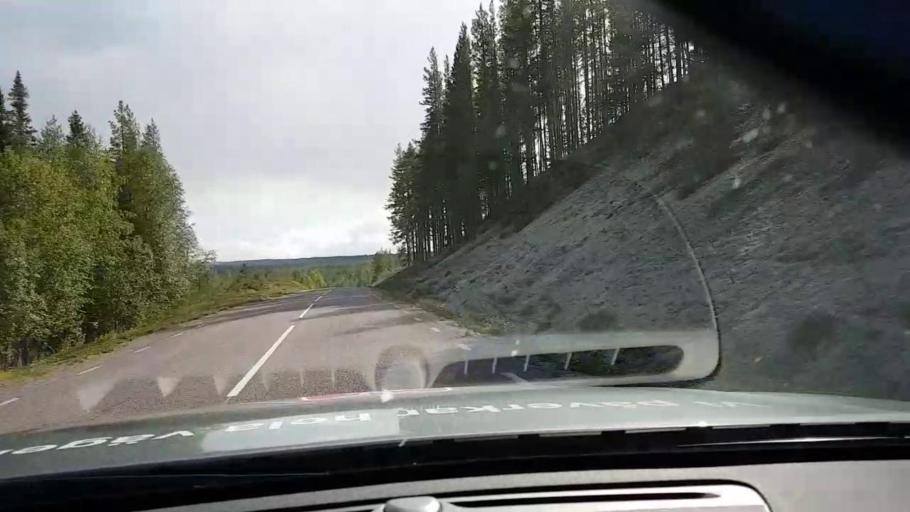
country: SE
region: Vaesterbotten
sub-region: Asele Kommun
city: Asele
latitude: 63.8743
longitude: 17.3567
